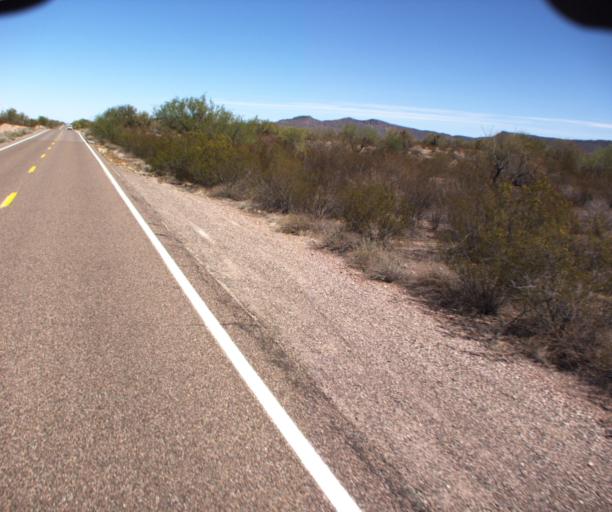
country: US
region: Arizona
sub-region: Pima County
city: Ajo
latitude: 32.1506
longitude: -112.7652
